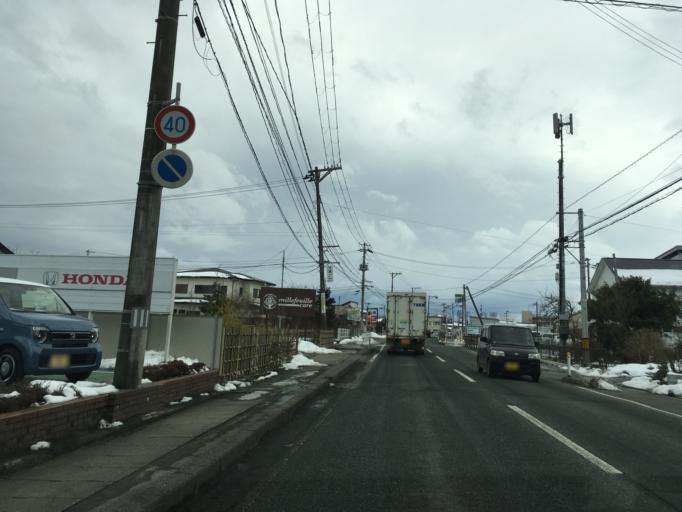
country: JP
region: Miyagi
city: Furukawa
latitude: 38.5840
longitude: 140.9668
